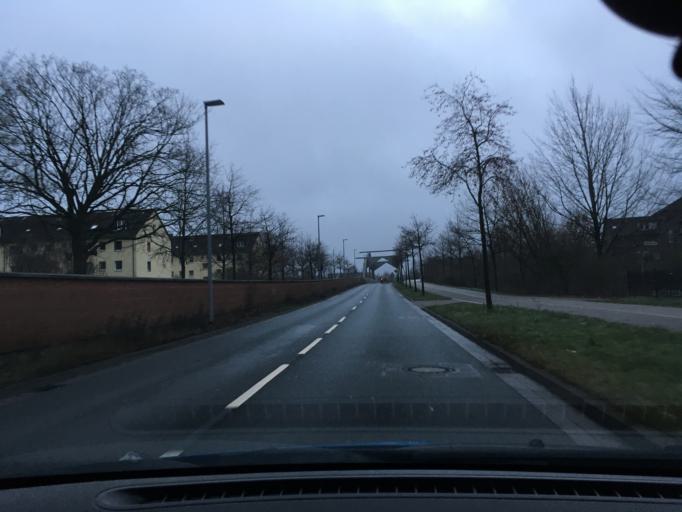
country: DE
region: Lower Saxony
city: Langenhagen
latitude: 52.4081
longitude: 9.7903
